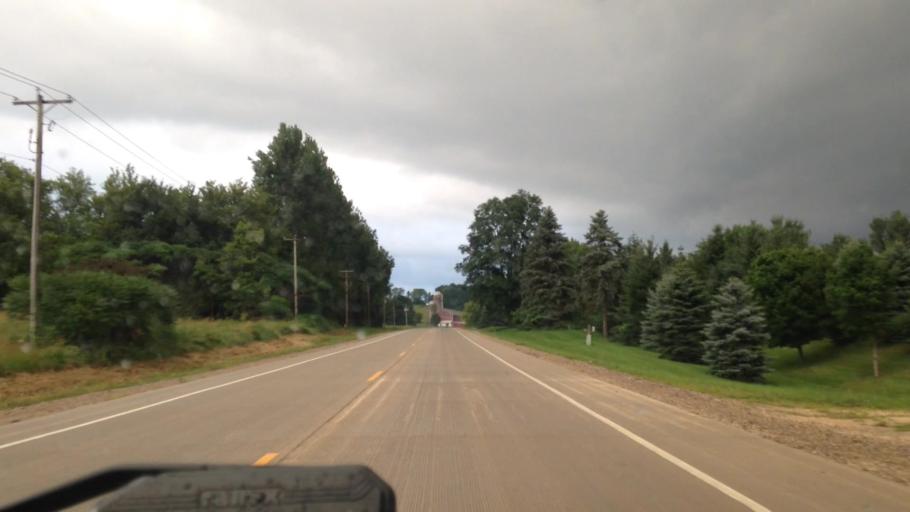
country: US
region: Wisconsin
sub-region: Dodge County
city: Mayville
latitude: 43.4610
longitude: -88.5614
